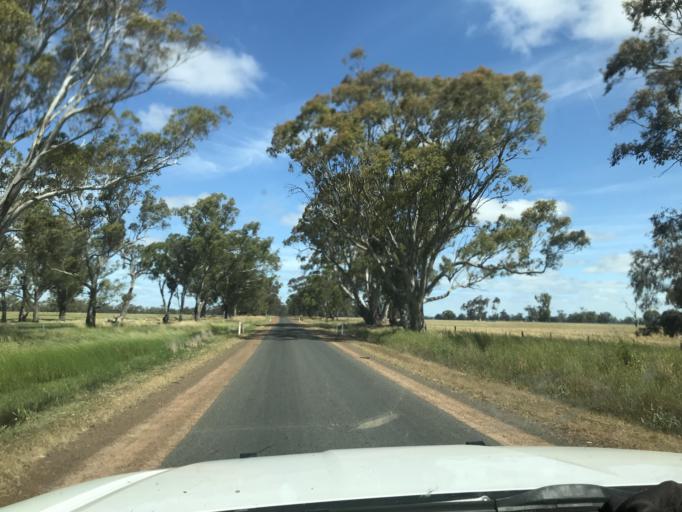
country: AU
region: South Australia
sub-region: Naracoorte and Lucindale
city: Naracoorte
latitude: -36.8448
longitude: 141.1572
